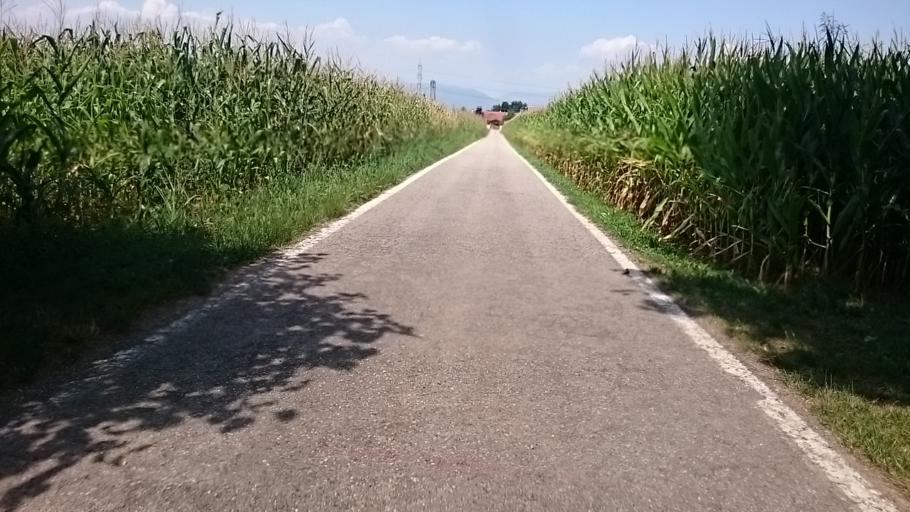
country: IT
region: Veneto
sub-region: Provincia di Padova
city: Fontaniva
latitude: 45.6653
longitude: 11.7495
